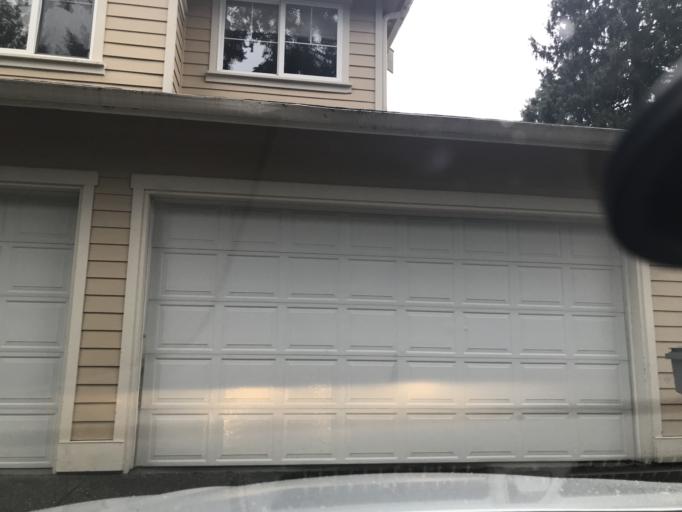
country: US
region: Washington
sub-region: King County
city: Kirkland
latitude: 47.6640
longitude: -122.1847
